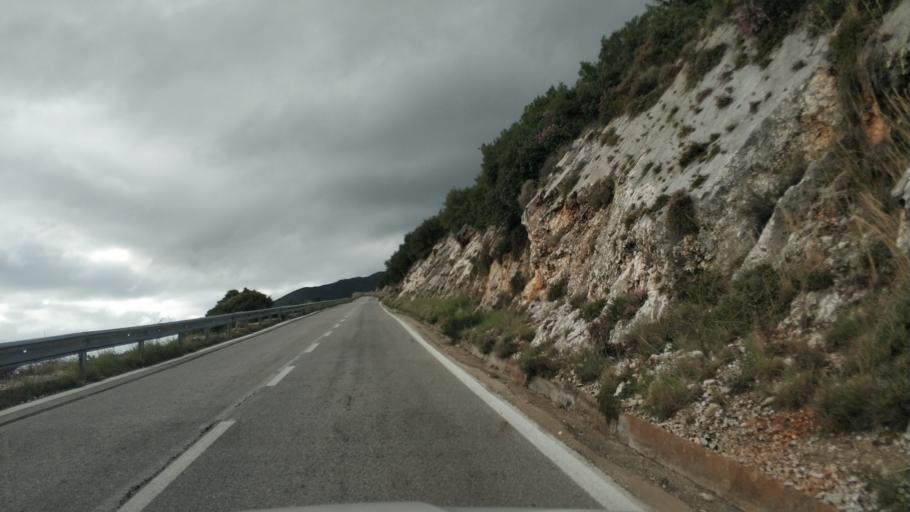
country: AL
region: Vlore
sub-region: Rrethi i Vlores
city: Vranisht
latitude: 40.1783
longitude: 19.5992
